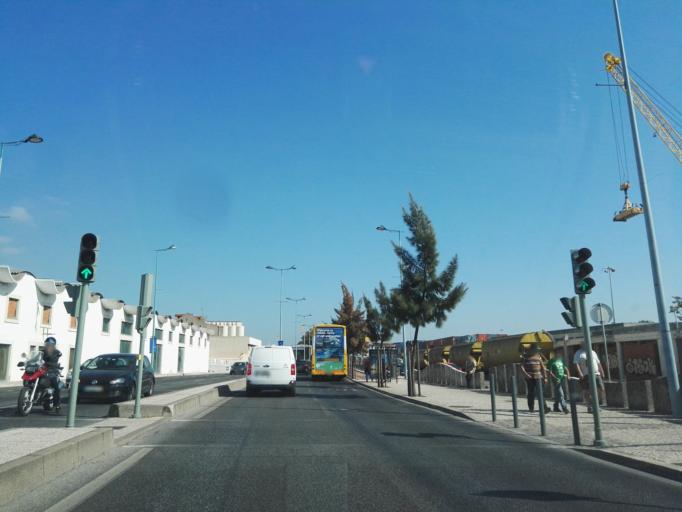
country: PT
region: Lisbon
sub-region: Lisbon
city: Lisbon
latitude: 38.7267
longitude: -9.1099
